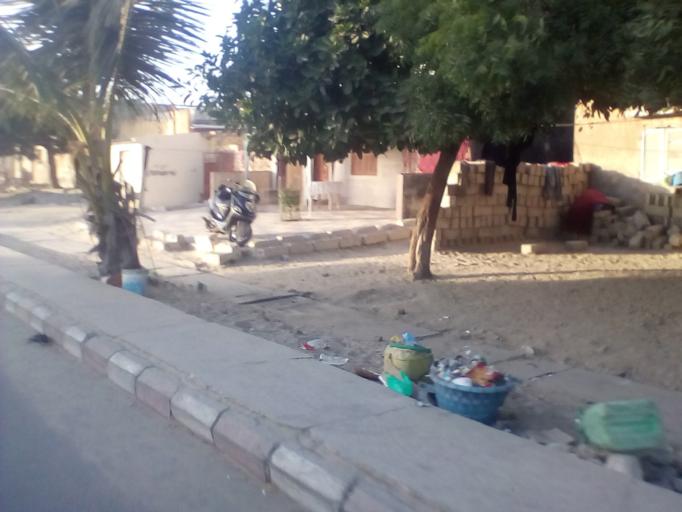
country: SN
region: Saint-Louis
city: Saint-Louis
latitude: 16.0191
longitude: -16.4944
